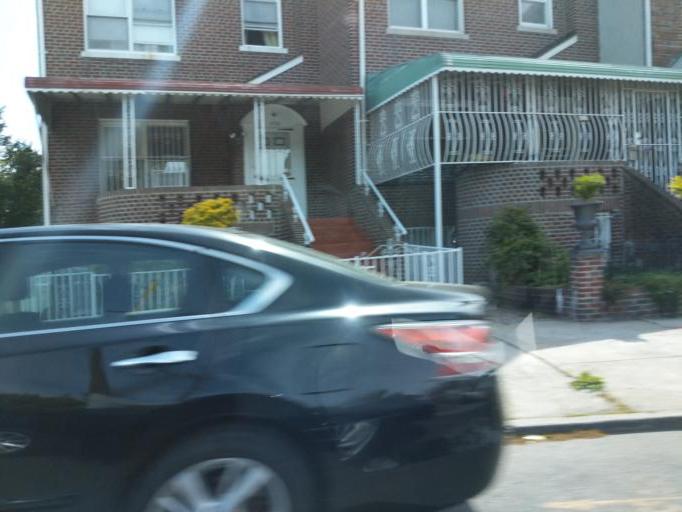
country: US
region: New York
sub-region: Kings County
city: Brooklyn
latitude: 40.6513
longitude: -73.9231
